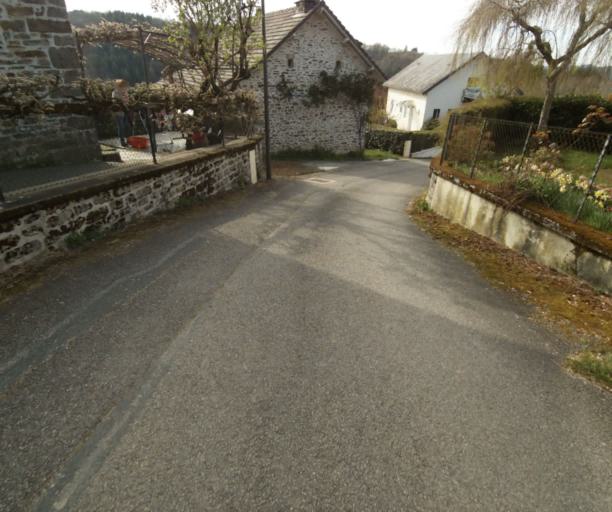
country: FR
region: Limousin
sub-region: Departement de la Correze
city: Correze
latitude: 45.4212
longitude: 1.8021
